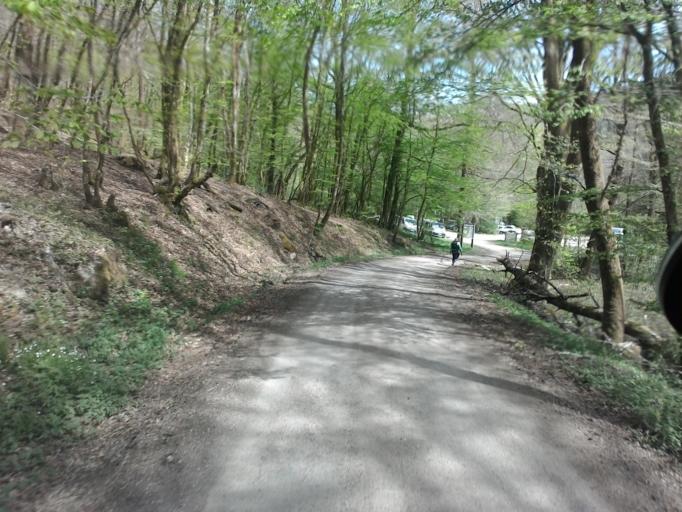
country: FR
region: Bourgogne
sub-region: Departement de la Nievre
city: Lormes
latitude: 47.3084
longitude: 3.9175
